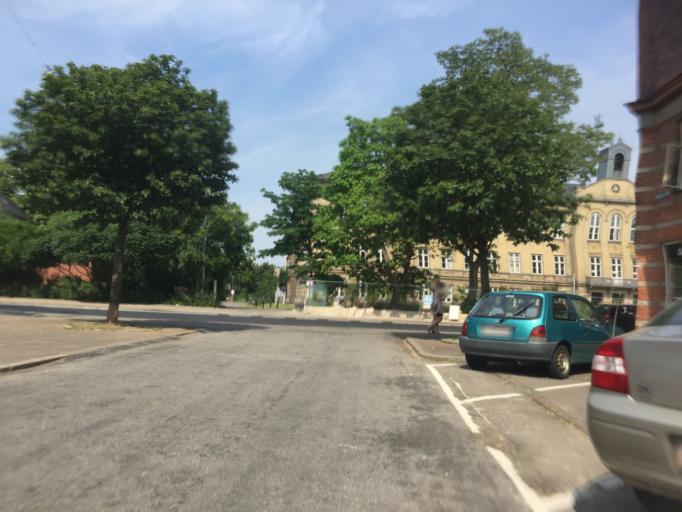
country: DK
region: Capital Region
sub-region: Frederiksberg Kommune
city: Frederiksberg
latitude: 55.6842
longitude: 12.5422
